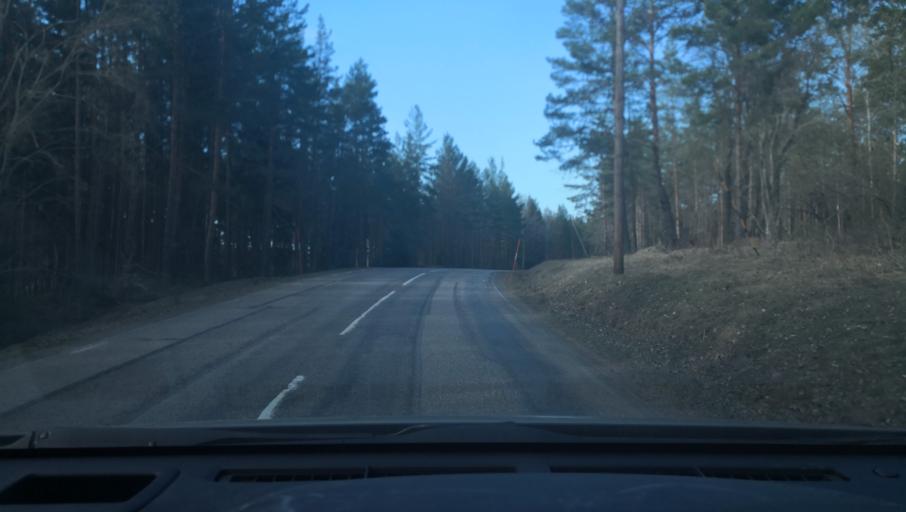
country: SE
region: Uppsala
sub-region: Heby Kommun
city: Morgongava
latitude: 59.9900
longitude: 16.9150
